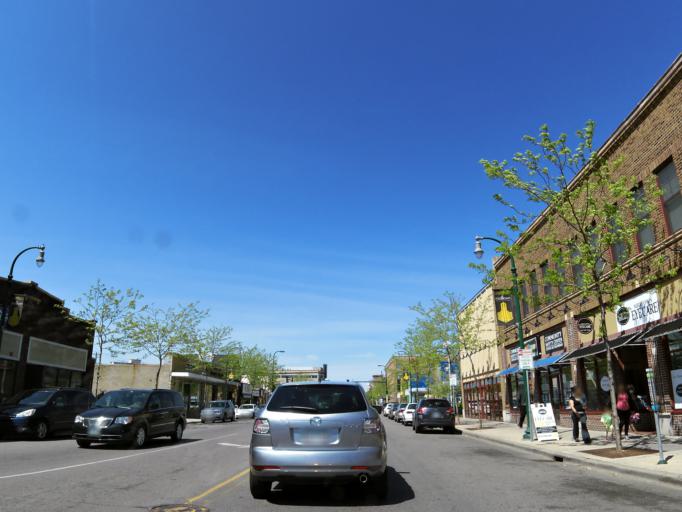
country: US
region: Minnesota
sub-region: Hennepin County
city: Minneapolis
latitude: 44.9485
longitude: -93.2626
